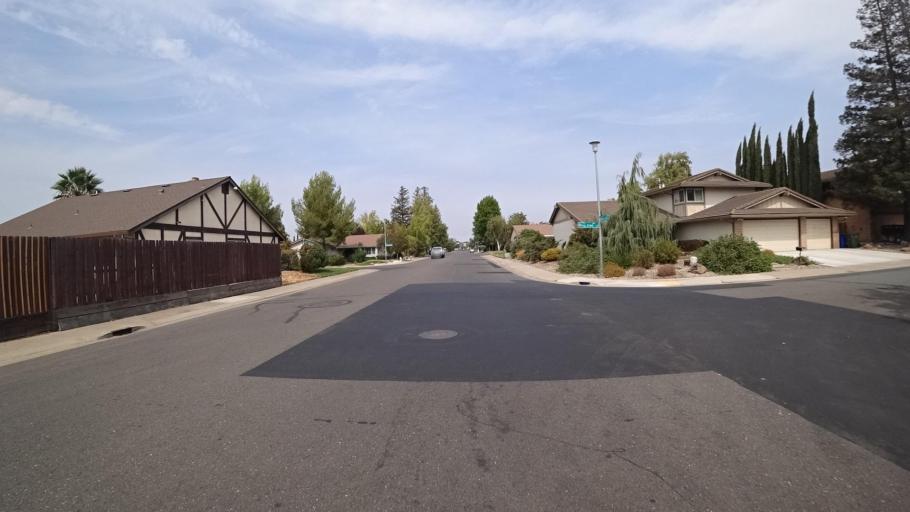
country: US
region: California
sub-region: Sacramento County
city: Elk Grove
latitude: 38.4203
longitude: -121.3878
